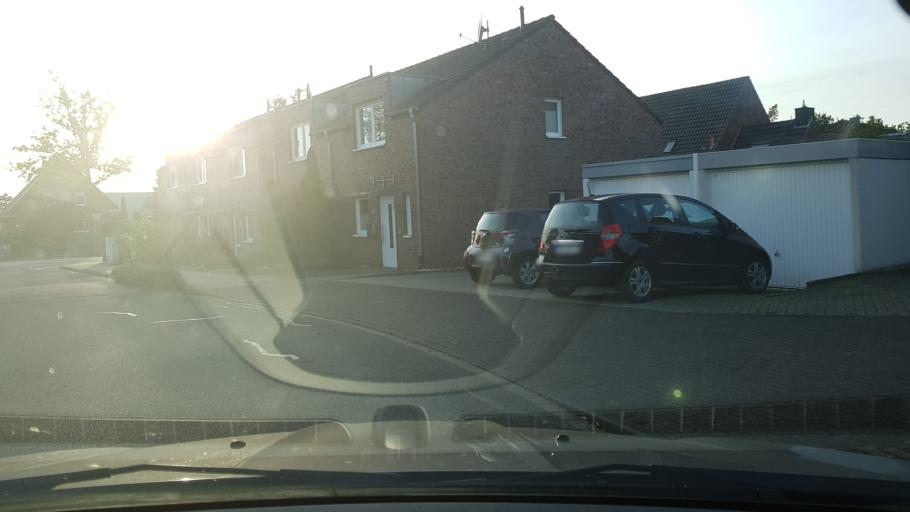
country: DE
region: North Rhine-Westphalia
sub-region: Regierungsbezirk Munster
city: Rhede
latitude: 51.8346
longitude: 6.7101
